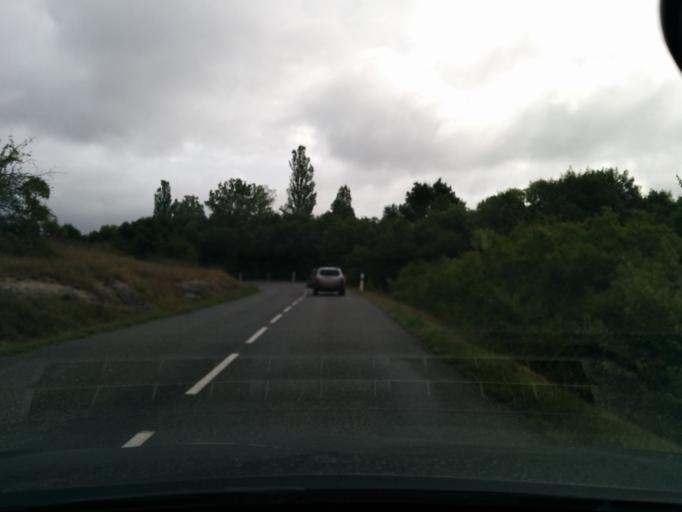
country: FR
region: Midi-Pyrenees
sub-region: Departement du Lot
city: Luzech
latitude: 44.3836
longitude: 1.3173
